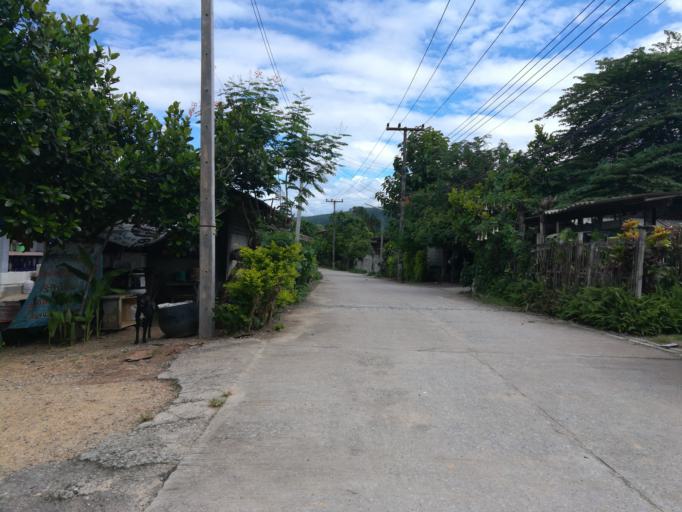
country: TH
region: Chiang Mai
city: Chom Thong
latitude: 18.4065
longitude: 98.6496
